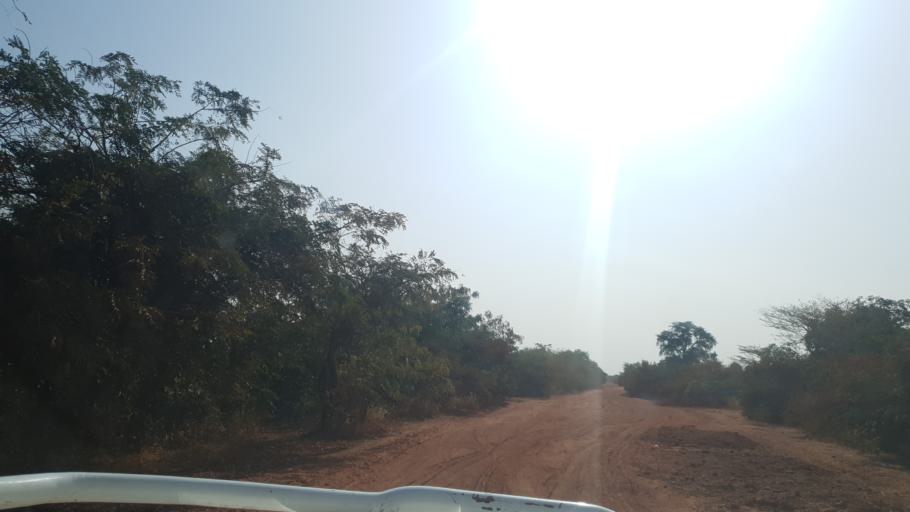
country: ML
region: Koulikoro
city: Dioila
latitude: 12.6976
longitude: -6.7584
